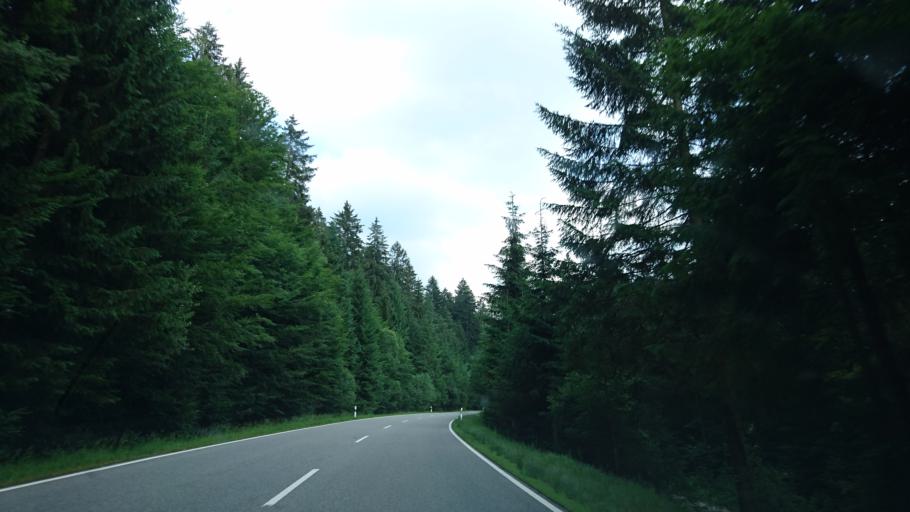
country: DE
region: Bavaria
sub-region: Lower Bavaria
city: Spiegelau
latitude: 48.9232
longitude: 13.4183
